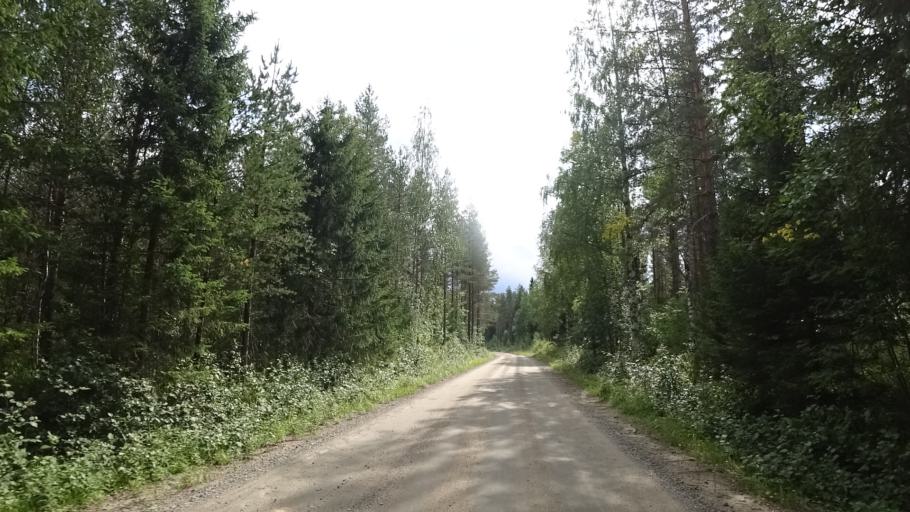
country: FI
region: North Karelia
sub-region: Joensuu
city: Ilomantsi
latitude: 62.9246
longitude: 31.3331
